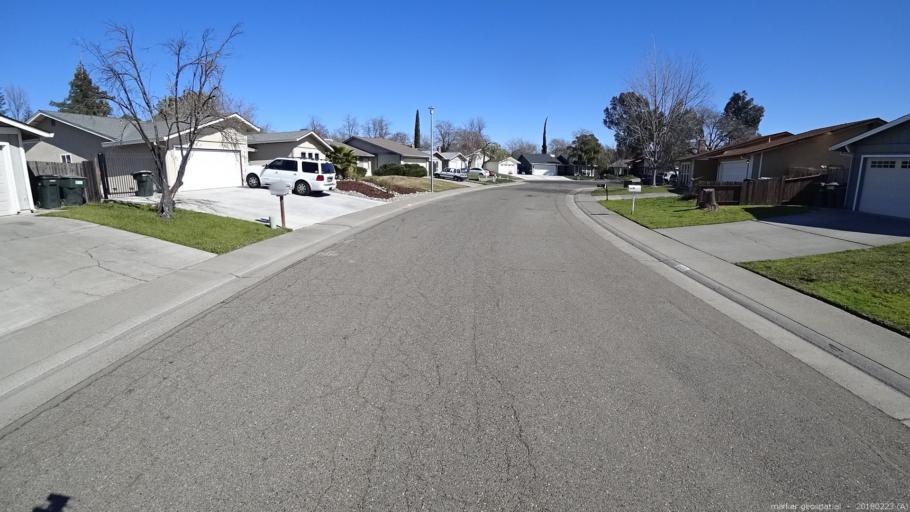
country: US
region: California
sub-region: Sacramento County
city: North Highlands
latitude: 38.7115
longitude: -121.3900
